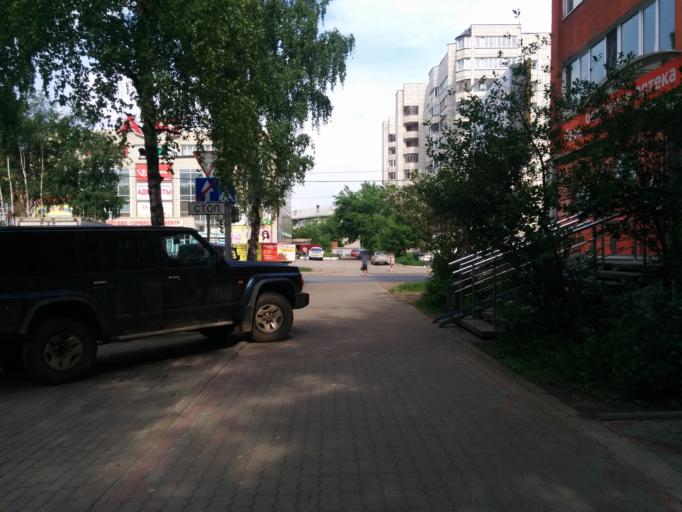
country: RU
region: Perm
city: Perm
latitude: 58.0168
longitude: 56.2920
